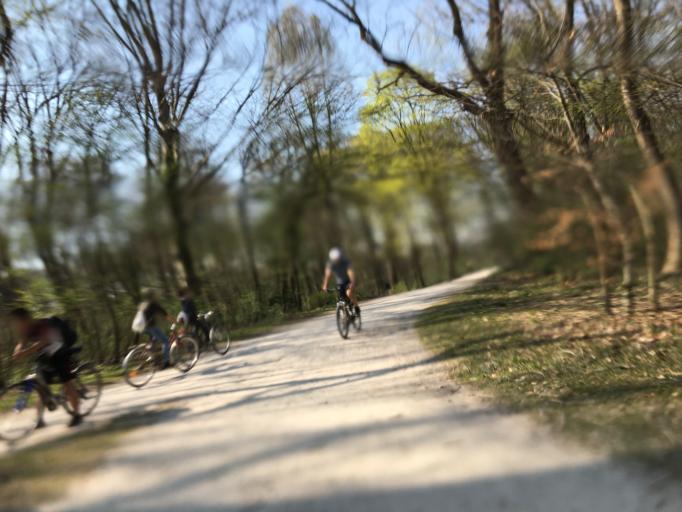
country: DE
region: Bavaria
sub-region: Upper Bavaria
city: Unterfoehring
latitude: 48.1826
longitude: 11.6240
